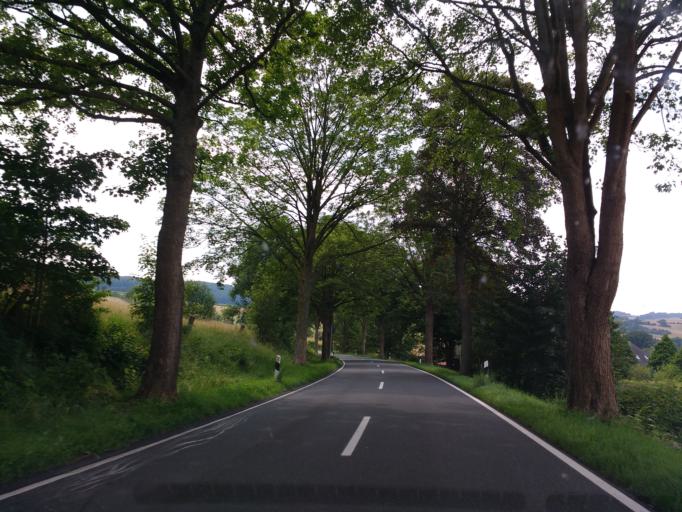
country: DE
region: Lower Saxony
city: Bad Pyrmont
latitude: 52.0109
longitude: 9.2067
